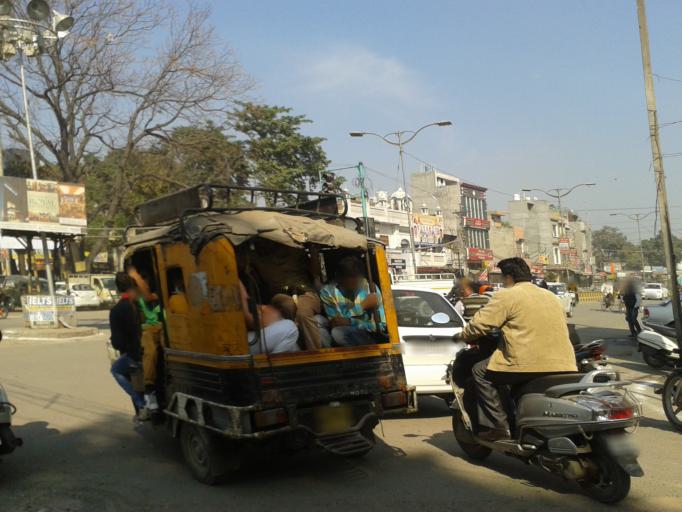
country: IN
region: Punjab
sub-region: Amritsar
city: Amritsar
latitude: 31.6306
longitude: 74.8730
